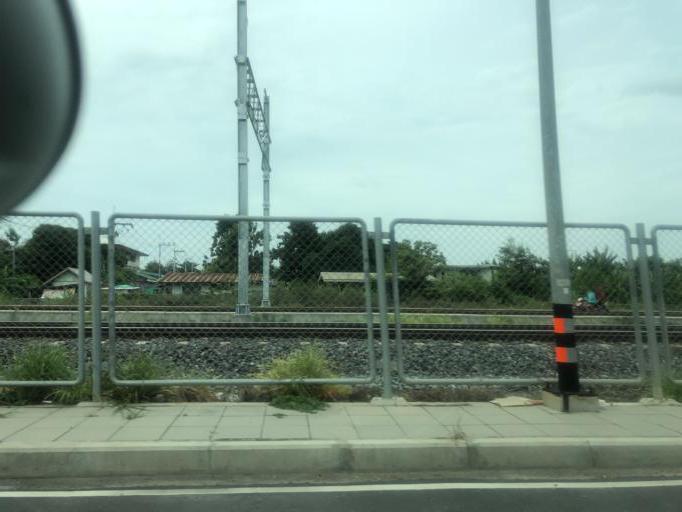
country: TH
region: Bangkok
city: Don Mueang
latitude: 13.9620
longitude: 100.6056
